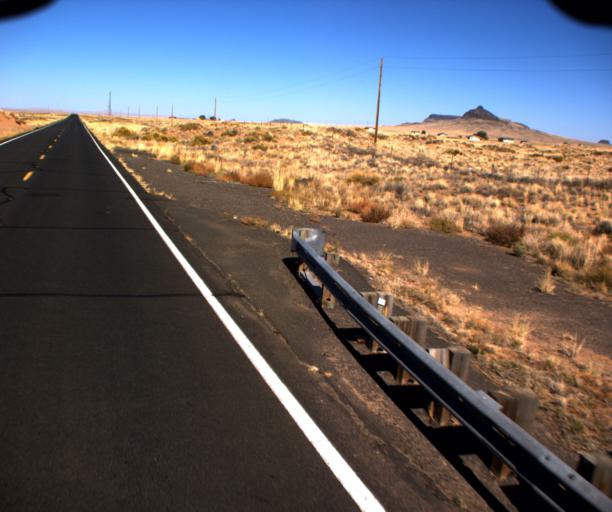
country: US
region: Arizona
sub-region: Navajo County
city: Dilkon
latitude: 35.5037
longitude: -110.4357
